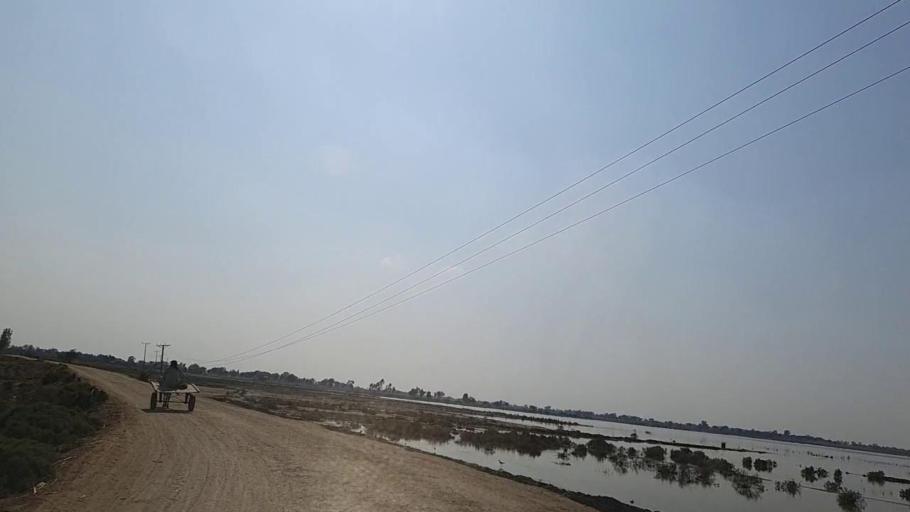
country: PK
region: Sindh
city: Daur
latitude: 26.4578
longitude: 68.2503
